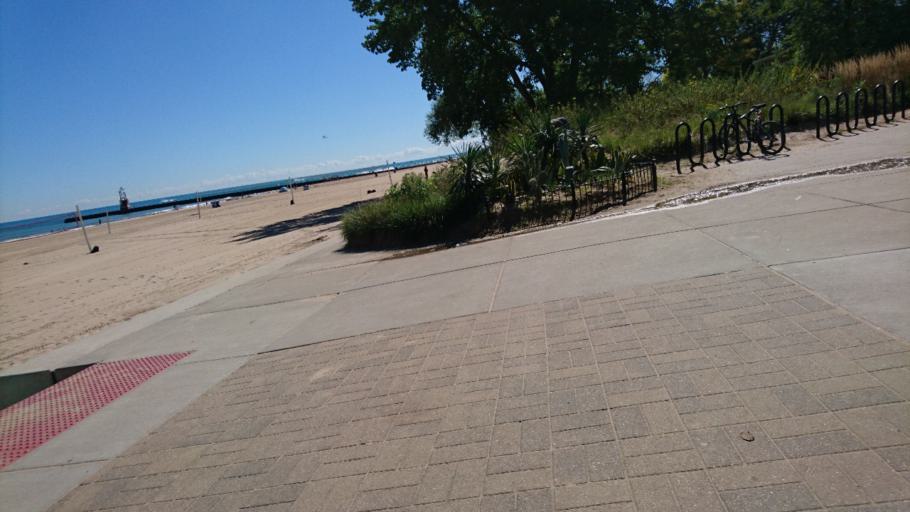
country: US
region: Illinois
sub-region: Cook County
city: Evanston
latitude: 41.9862
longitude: -87.6527
